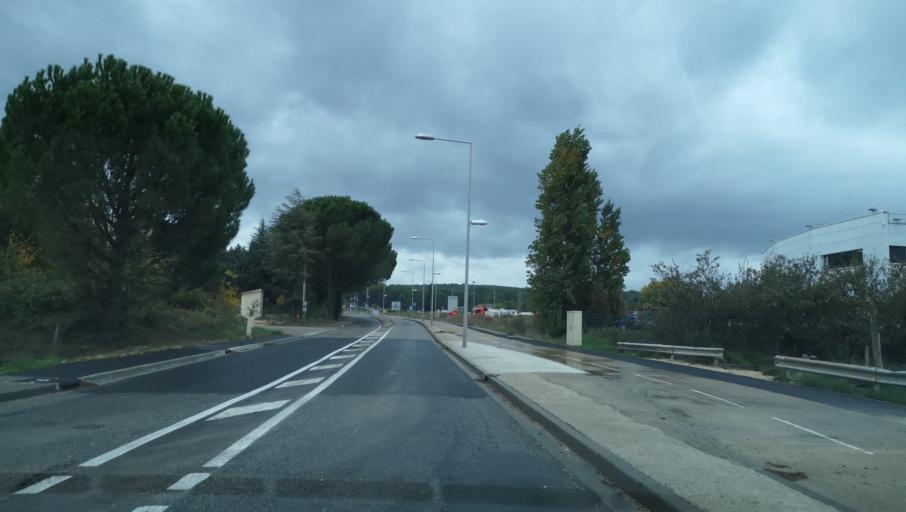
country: FR
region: Provence-Alpes-Cote d'Azur
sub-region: Departement des Bouches-du-Rhone
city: Rousset
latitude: 43.4666
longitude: 5.6124
